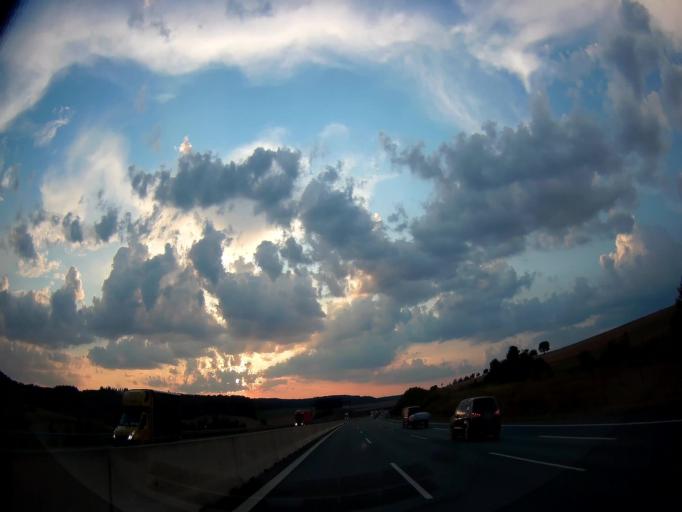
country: DE
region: Bavaria
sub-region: Regierungsbezirk Unterfranken
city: Waldbrunn
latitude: 49.7494
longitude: 9.8003
